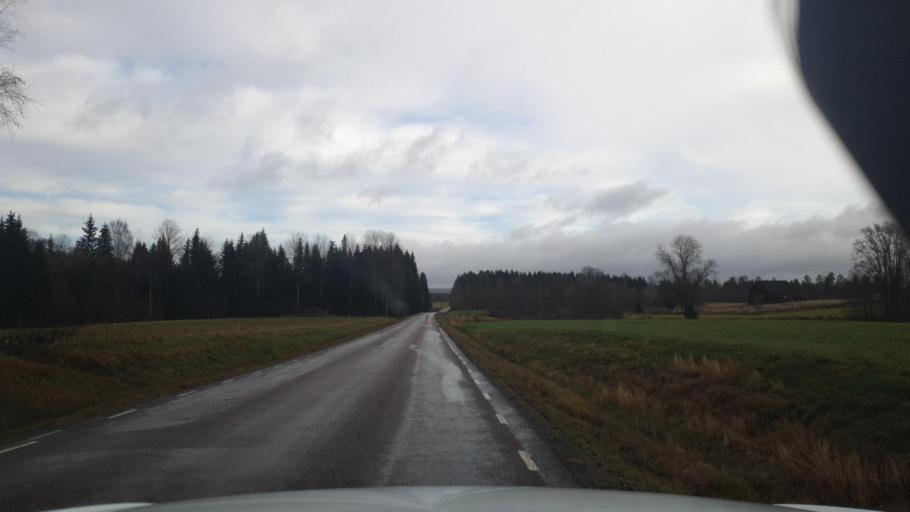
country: SE
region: Vaermland
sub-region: Eda Kommun
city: Charlottenberg
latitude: 59.7730
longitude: 12.1618
